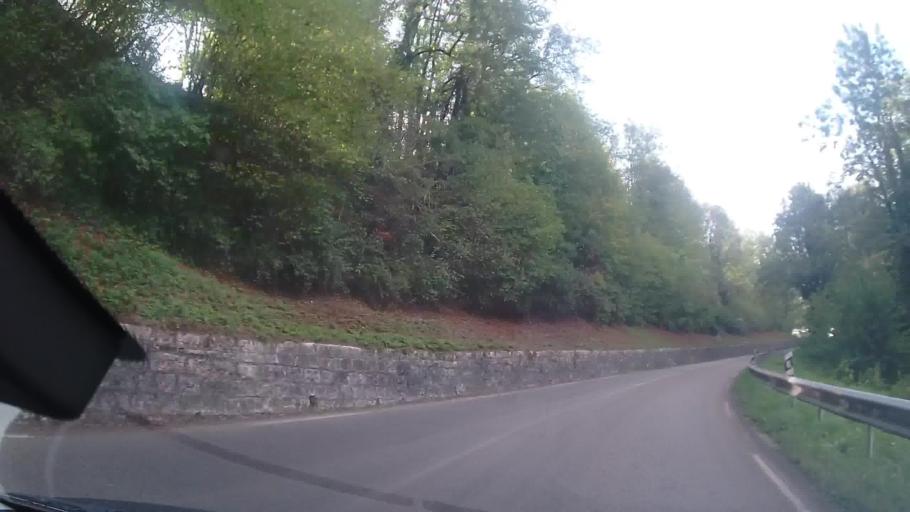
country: FR
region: Franche-Comte
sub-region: Departement du Jura
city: Clairvaux-les-Lacs
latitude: 46.5749
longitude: 5.7570
